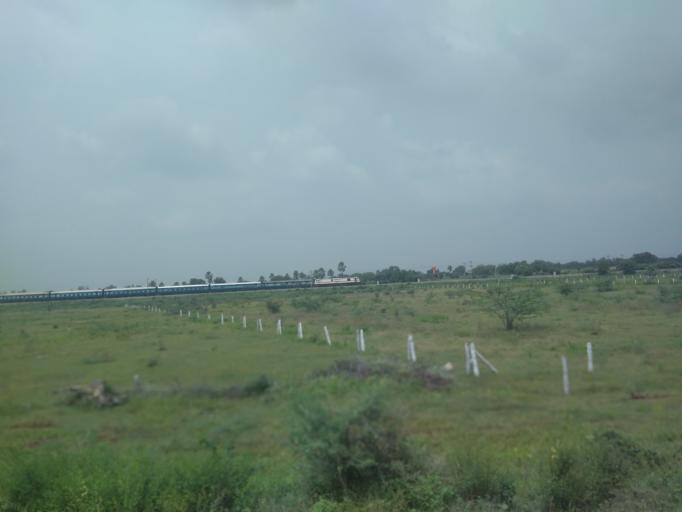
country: IN
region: Telangana
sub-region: Warangal
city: Jangaon
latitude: 17.6659
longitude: 79.0866
